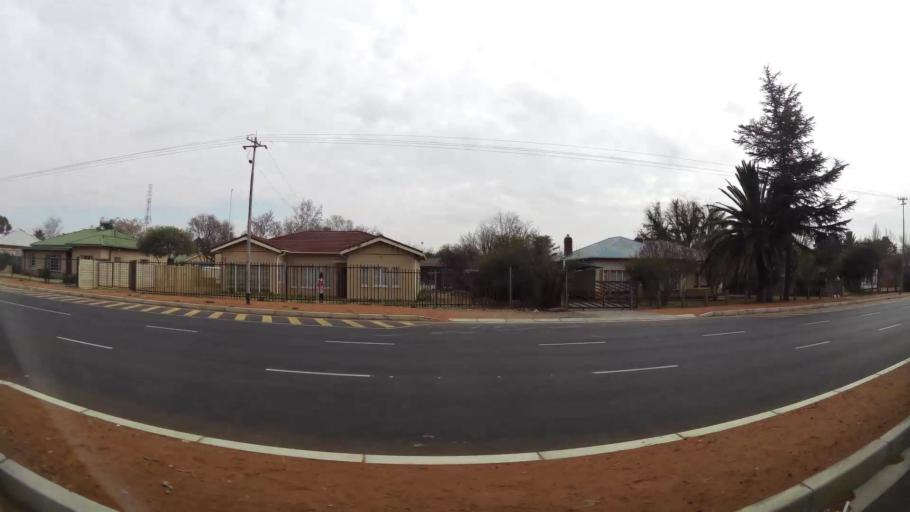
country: ZA
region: Orange Free State
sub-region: Mangaung Metropolitan Municipality
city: Bloemfontein
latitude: -29.1254
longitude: 26.1949
